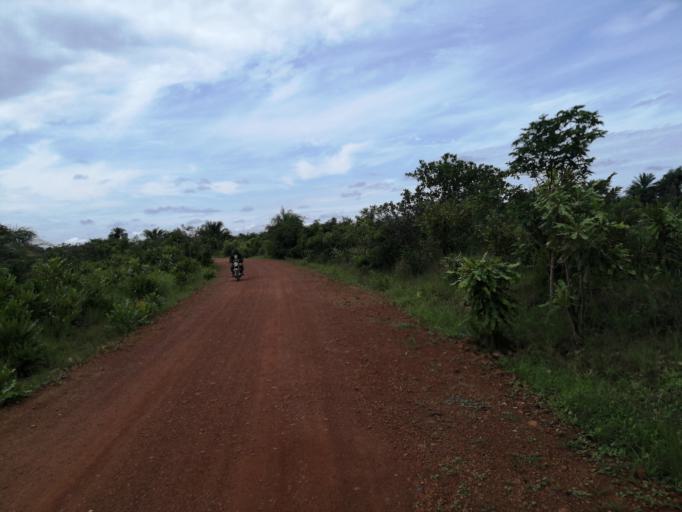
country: SL
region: Northern Province
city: Port Loko
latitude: 8.7698
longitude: -12.9133
